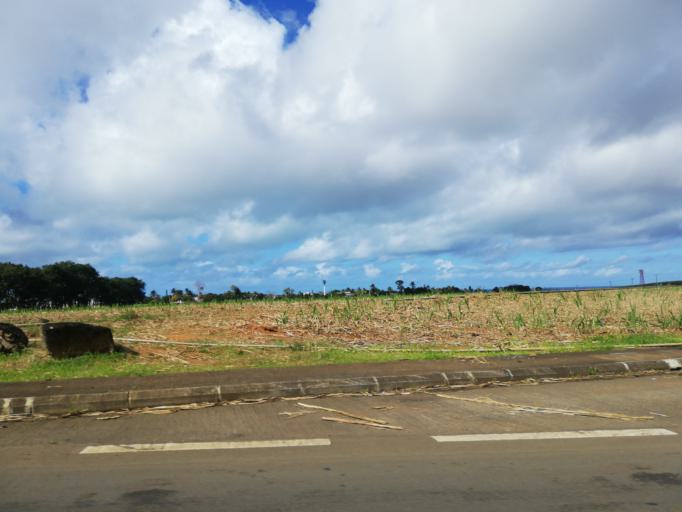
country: MU
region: Grand Port
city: Plaine Magnien
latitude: -20.4096
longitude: 57.6737
